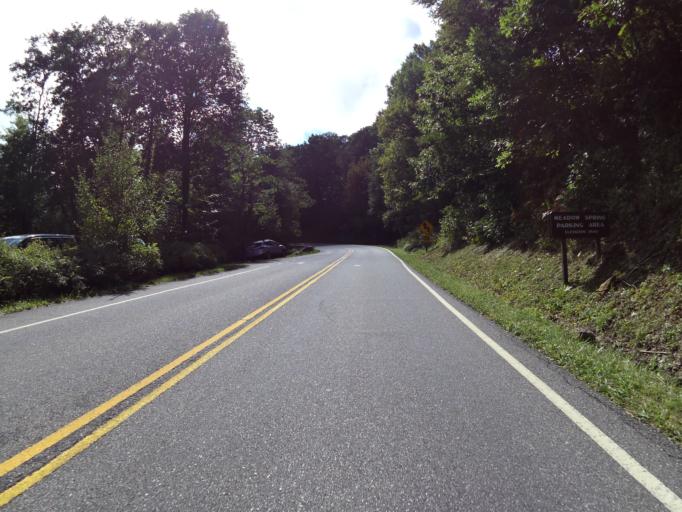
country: US
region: Virginia
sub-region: Page County
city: Luray
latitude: 38.6386
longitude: -78.3137
